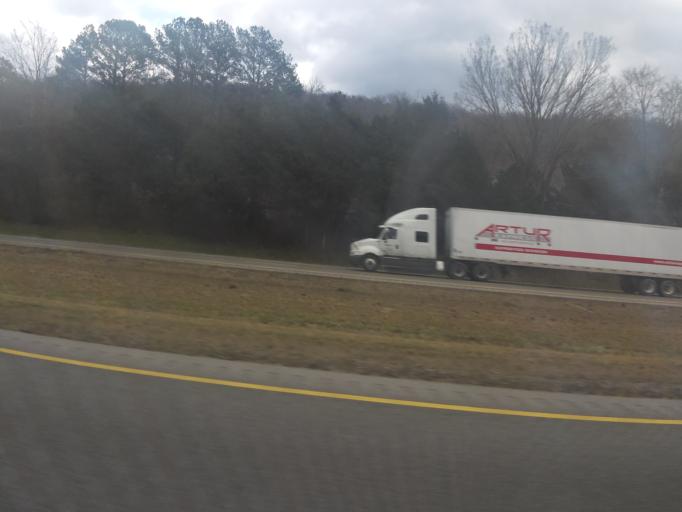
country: US
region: Tennessee
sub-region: Marion County
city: Kimball
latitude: 35.0937
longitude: -85.7371
